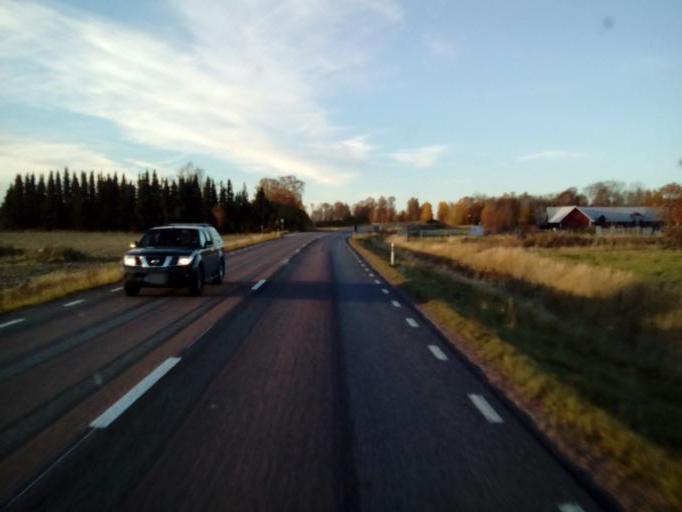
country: SE
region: OErebro
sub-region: Kumla Kommun
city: Hallabrottet
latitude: 59.1811
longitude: 15.2553
